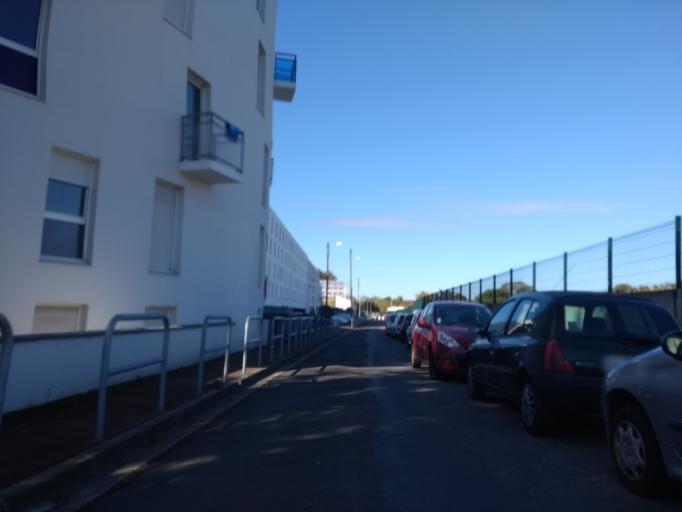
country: FR
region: Aquitaine
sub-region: Departement de la Gironde
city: Talence
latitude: 44.8083
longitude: -0.6014
